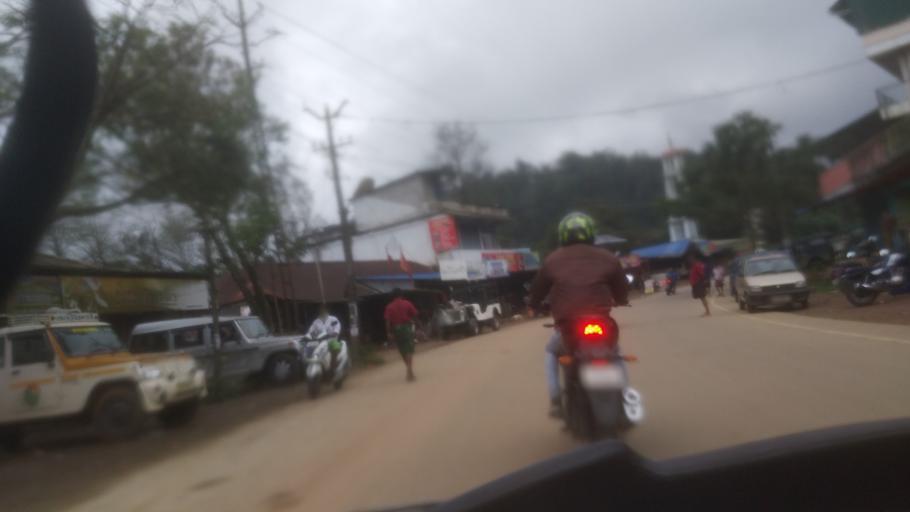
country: IN
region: Tamil Nadu
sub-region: Theni
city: Kombai
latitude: 9.8998
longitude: 77.1773
